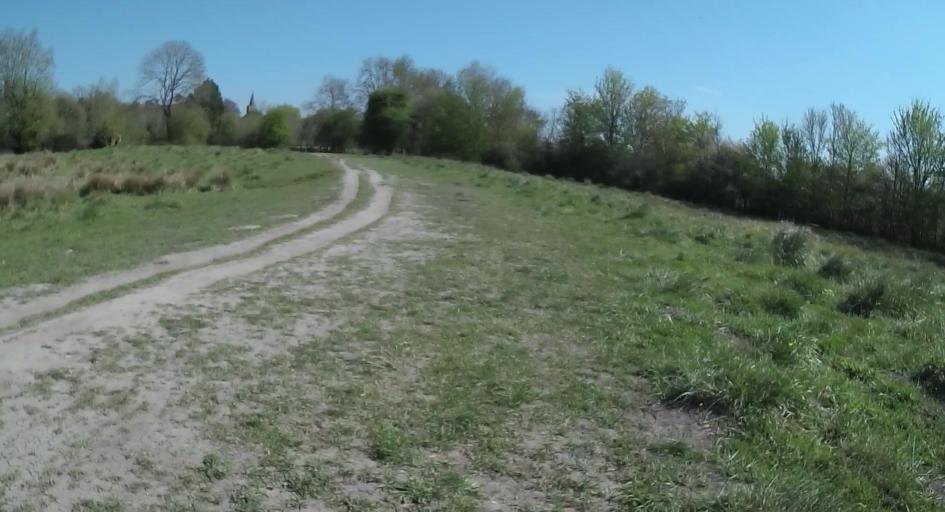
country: GB
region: England
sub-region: Hampshire
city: Compton
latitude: 51.0257
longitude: -1.3214
